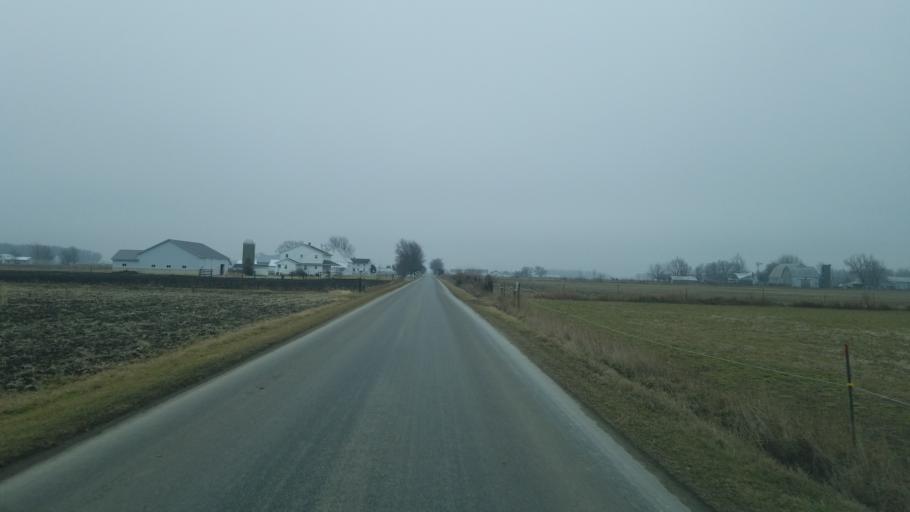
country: US
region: Indiana
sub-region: Adams County
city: Berne
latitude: 40.7216
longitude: -84.9174
